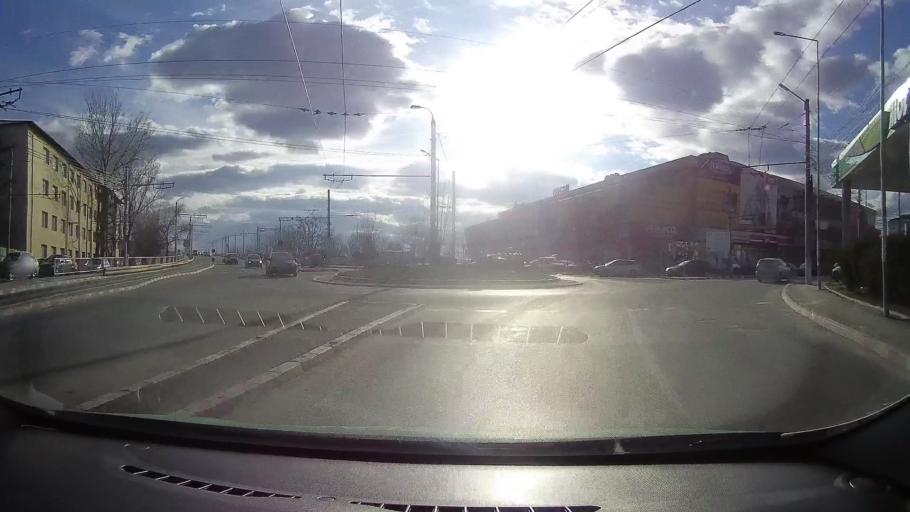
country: RO
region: Dambovita
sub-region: Comuna Lucieni
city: Lucieni
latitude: 44.8549
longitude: 25.4220
